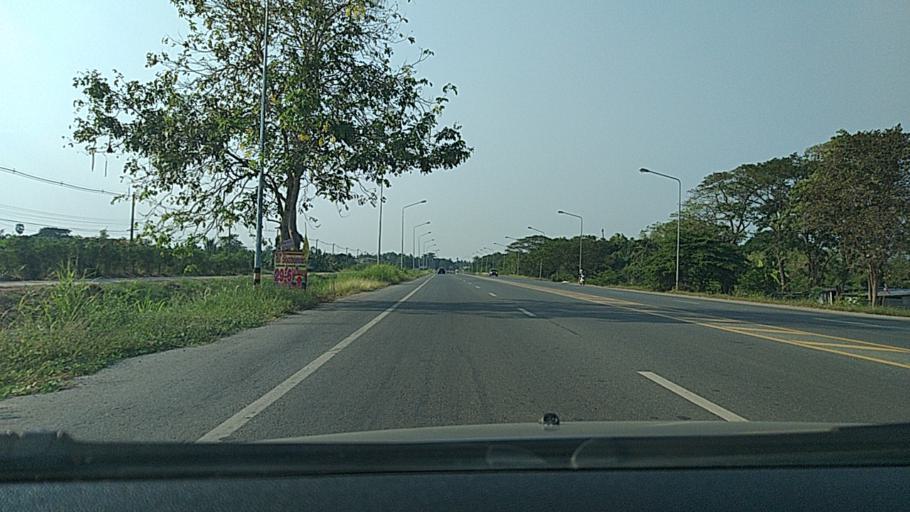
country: TH
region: Sing Buri
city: Sing Buri
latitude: 14.8570
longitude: 100.4101
